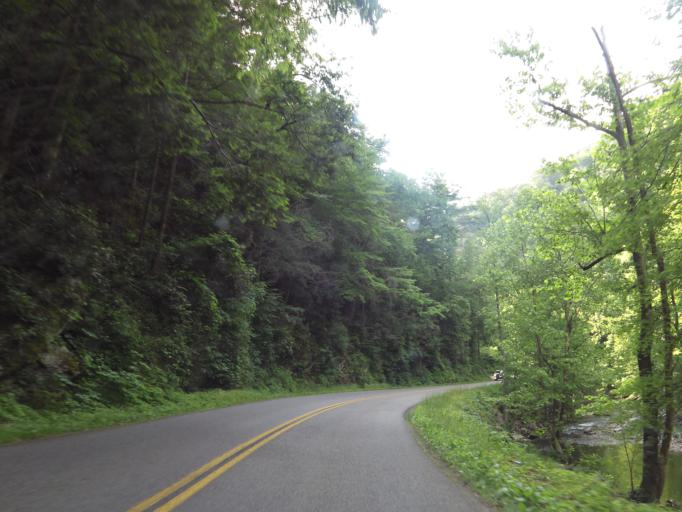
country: US
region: Tennessee
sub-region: Sevier County
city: Pigeon Forge
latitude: 35.6616
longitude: -83.7041
